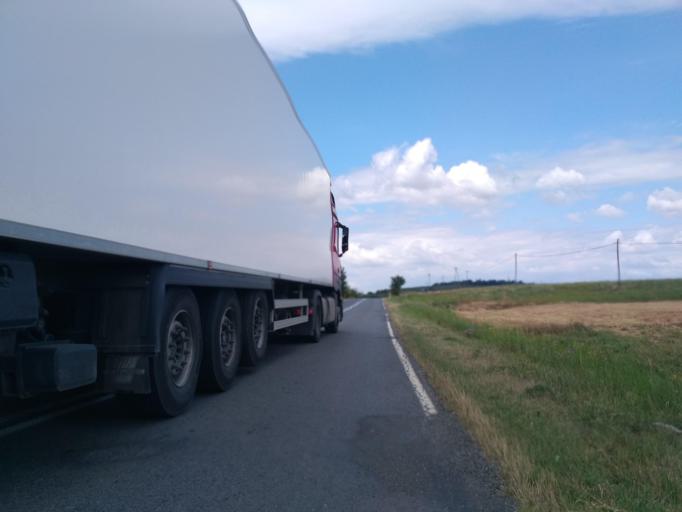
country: PL
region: Subcarpathian Voivodeship
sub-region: Powiat przeworski
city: Jawornik Polski
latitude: 49.8870
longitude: 22.2416
